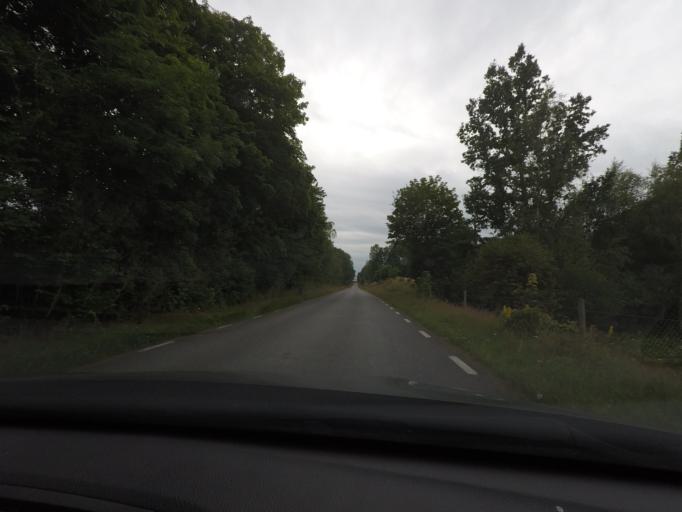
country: SE
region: Skane
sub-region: Osby Kommun
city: Osby
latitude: 56.4255
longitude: 13.8324
